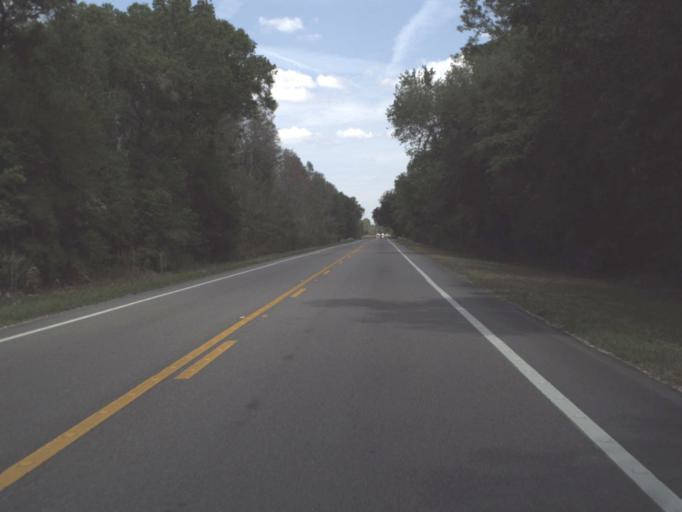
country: US
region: Florida
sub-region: Hernando County
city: Ridge Manor
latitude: 28.5348
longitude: -82.0908
